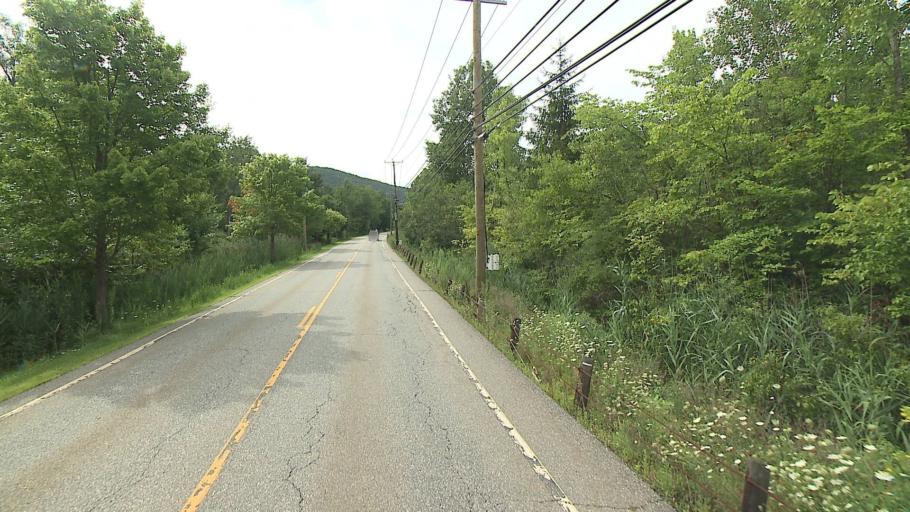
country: US
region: Connecticut
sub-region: Litchfield County
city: Kent
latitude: 41.7204
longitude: -73.4734
